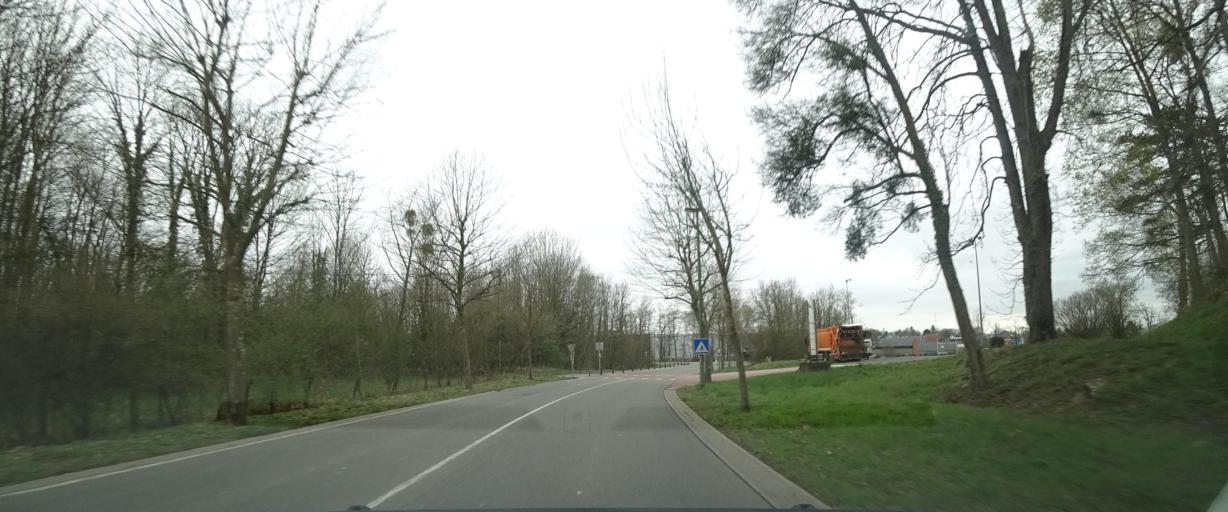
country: BE
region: Wallonia
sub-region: Province du Luxembourg
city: Marche-en-Famenne
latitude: 50.2201
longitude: 5.3346
